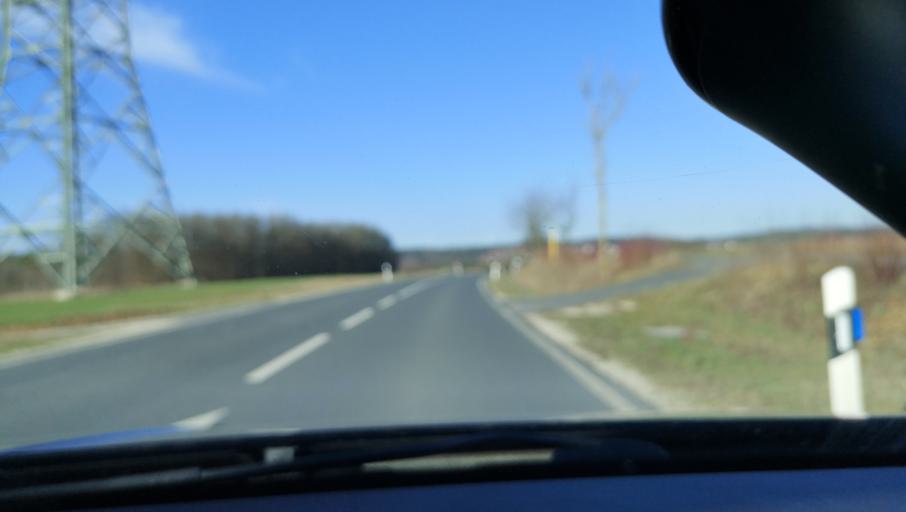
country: DE
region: Bavaria
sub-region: Upper Franconia
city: Sonnefeld
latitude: 50.2128
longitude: 11.1142
